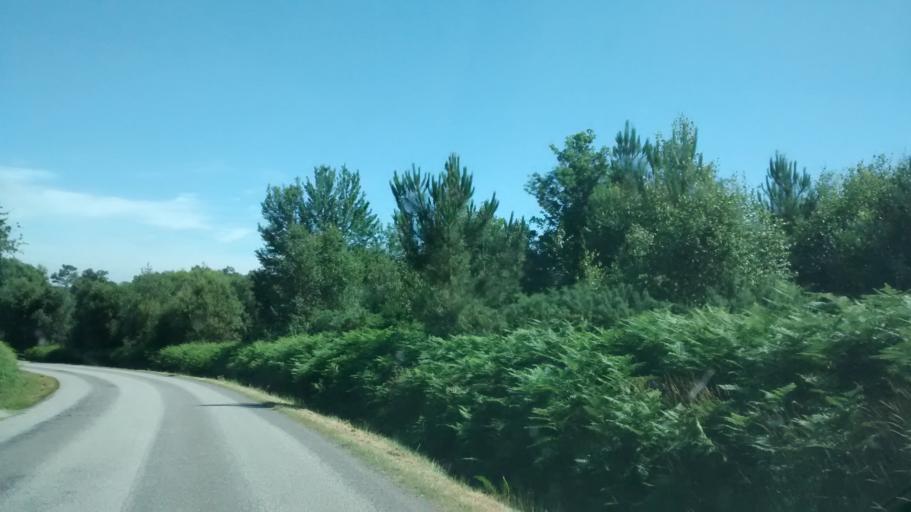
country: FR
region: Brittany
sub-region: Departement du Morbihan
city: Campeneac
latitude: 47.9902
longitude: -2.3057
